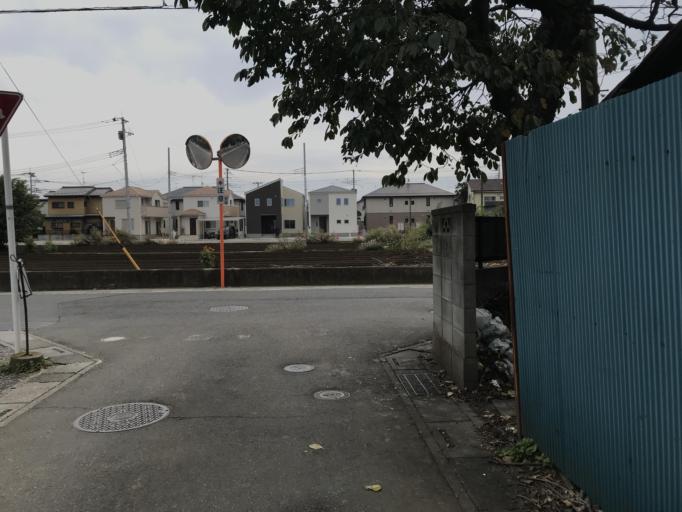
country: JP
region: Saitama
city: Shiraoka
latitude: 36.0174
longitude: 139.6585
